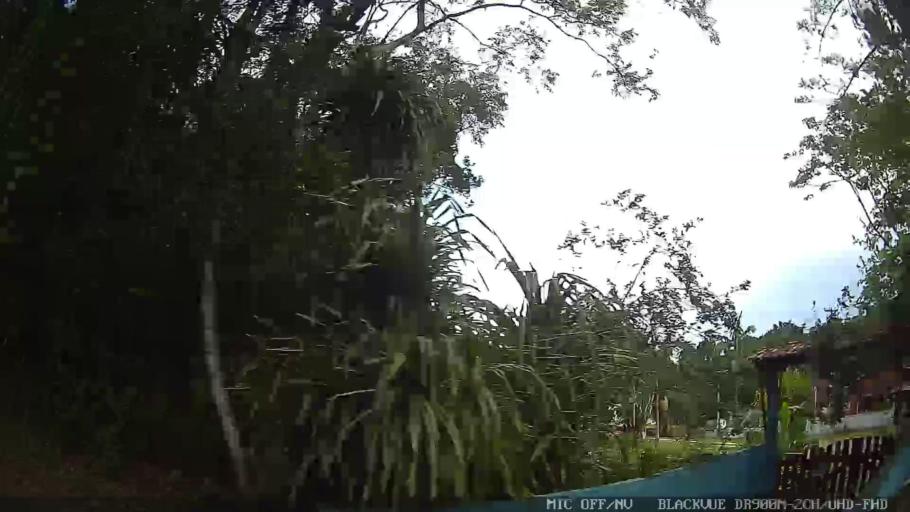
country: BR
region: Sao Paulo
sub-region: Iguape
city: Iguape
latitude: -24.6725
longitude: -47.4476
